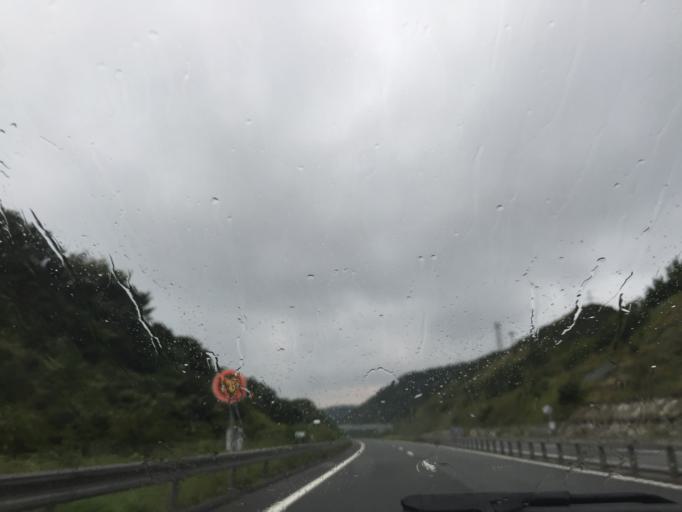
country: JP
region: Tokushima
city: Narutocho-mitsuishi
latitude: 34.2313
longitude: 134.6340
